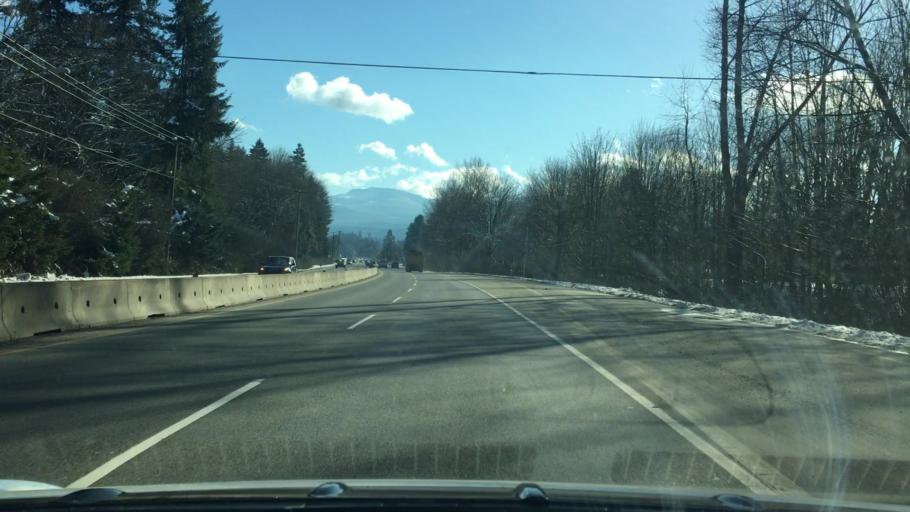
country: CA
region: British Columbia
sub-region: Cowichan Valley Regional District
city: Ladysmith
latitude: 49.0611
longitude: -123.8777
